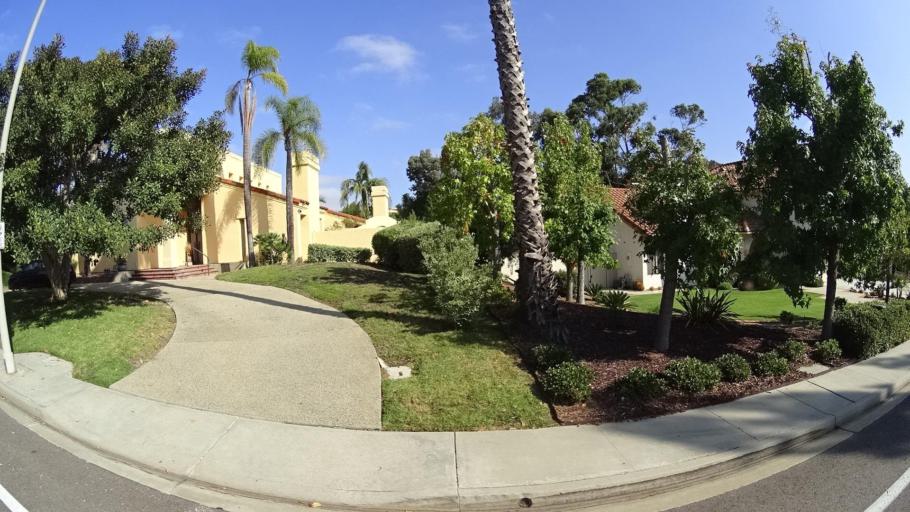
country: US
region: California
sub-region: San Diego County
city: Vista
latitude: 33.1717
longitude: -117.2318
